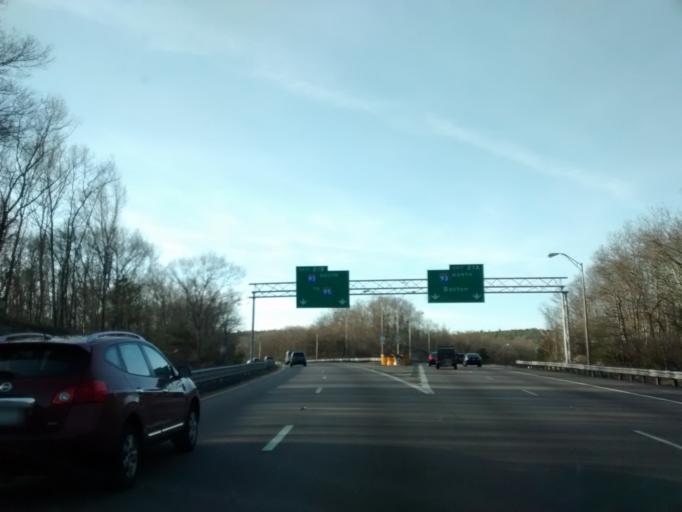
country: US
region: Massachusetts
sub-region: Norfolk County
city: Randolph
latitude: 42.1987
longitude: -71.0778
